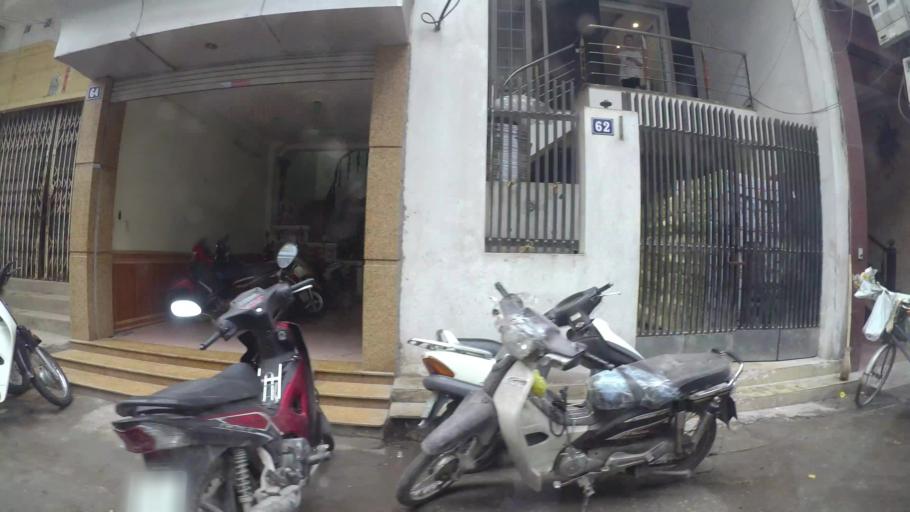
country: VN
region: Ha Noi
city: Hoan Kiem
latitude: 21.0384
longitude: 105.8548
